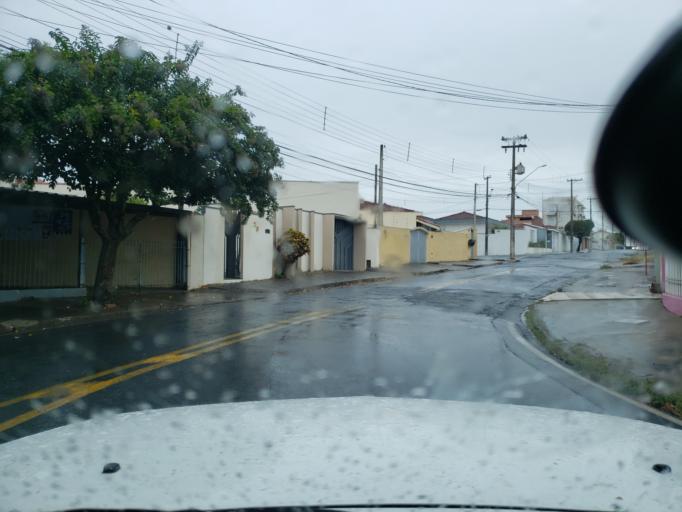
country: BR
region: Sao Paulo
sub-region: Moji-Guacu
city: Mogi-Gaucu
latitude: -22.3800
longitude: -46.9358
